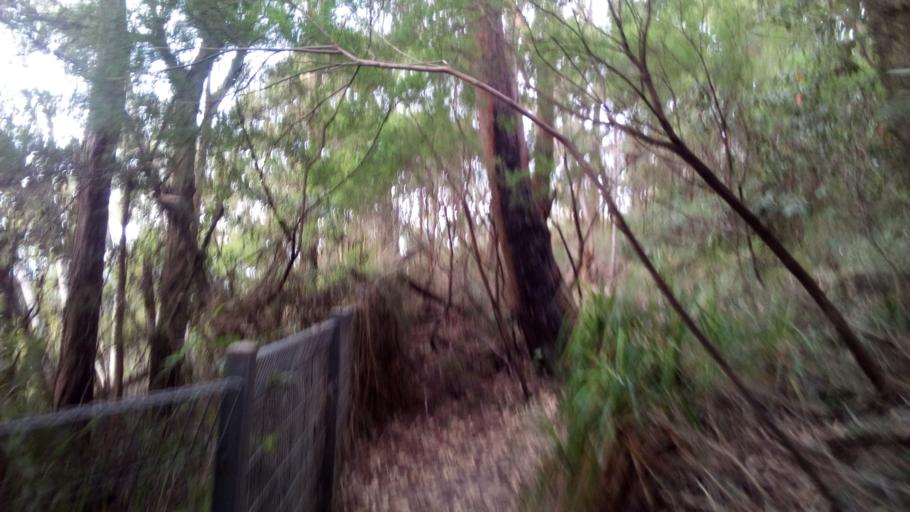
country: AU
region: New South Wales
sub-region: Wollongong
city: Mount Keira
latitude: -34.4037
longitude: 150.8563
